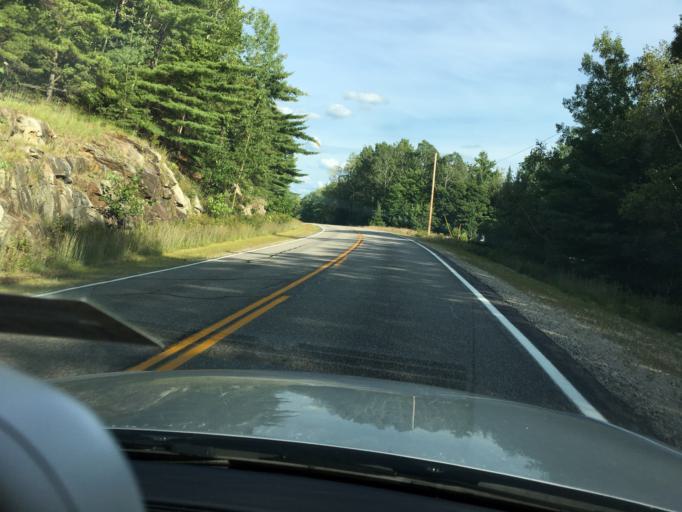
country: US
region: Maine
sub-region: Oxford County
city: Brownfield
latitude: 43.9306
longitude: -70.8821
